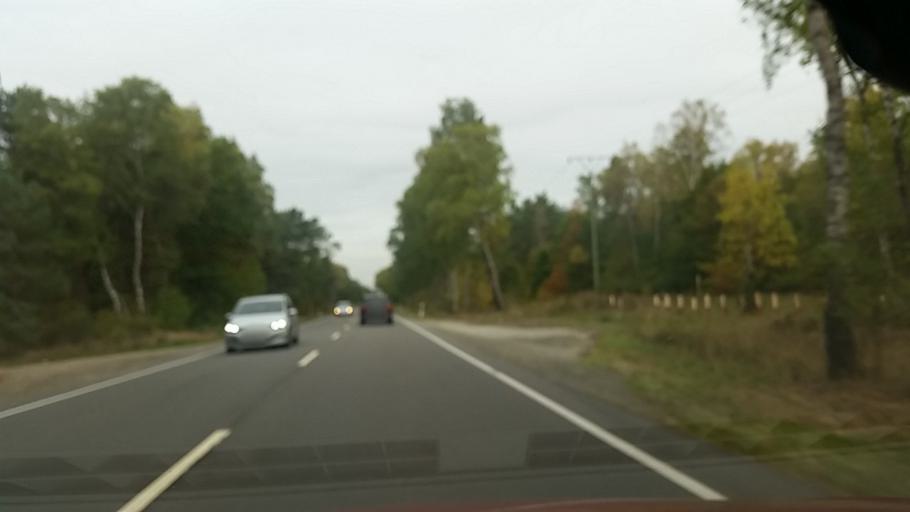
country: DE
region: Lower Saxony
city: Wesendorf
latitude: 52.5788
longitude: 10.4994
